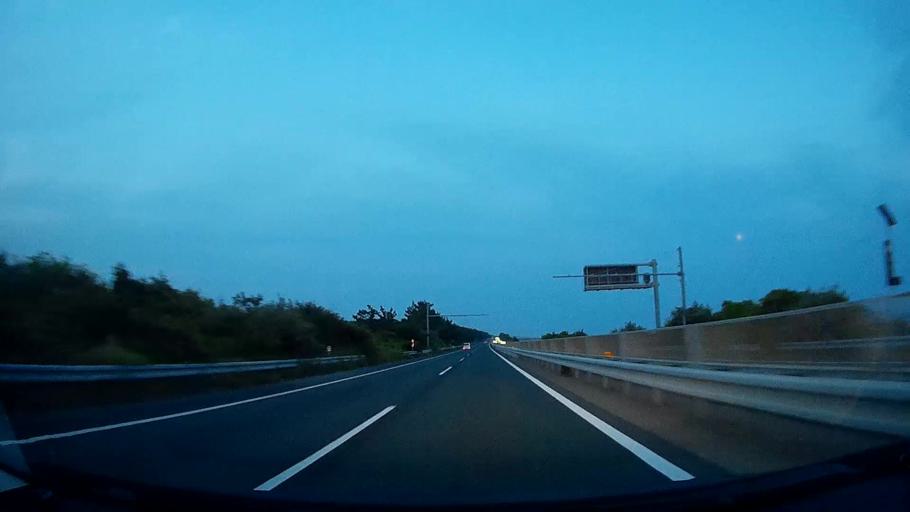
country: JP
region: Shizuoka
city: Kosai-shi
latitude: 34.6786
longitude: 137.6075
